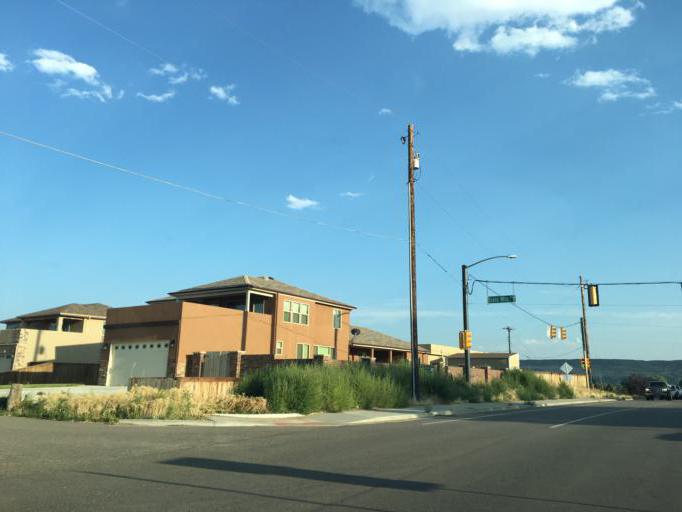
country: US
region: Colorado
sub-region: Jefferson County
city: Applewood
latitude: 39.7835
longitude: -105.1747
